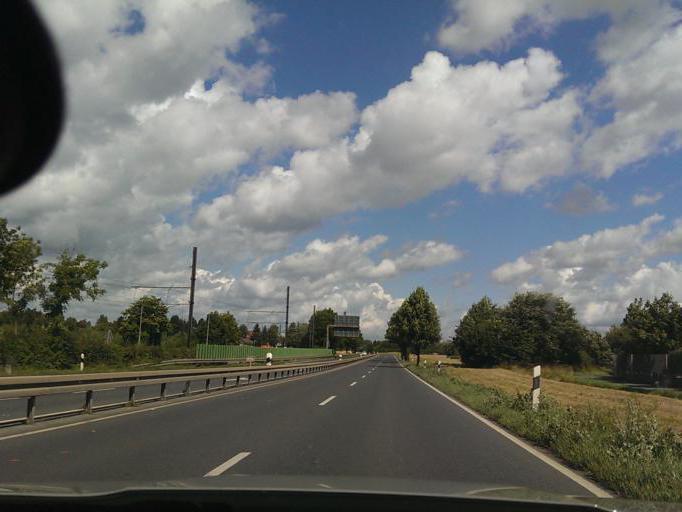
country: DE
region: Lower Saxony
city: Sarstedt
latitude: 52.2542
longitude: 9.8600
